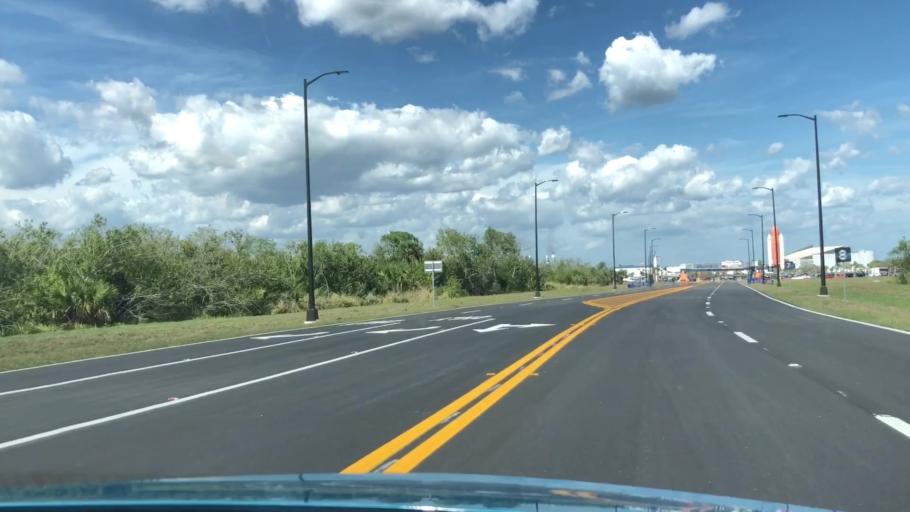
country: US
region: Florida
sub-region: Brevard County
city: Merritt Island
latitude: 28.5157
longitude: -80.6819
